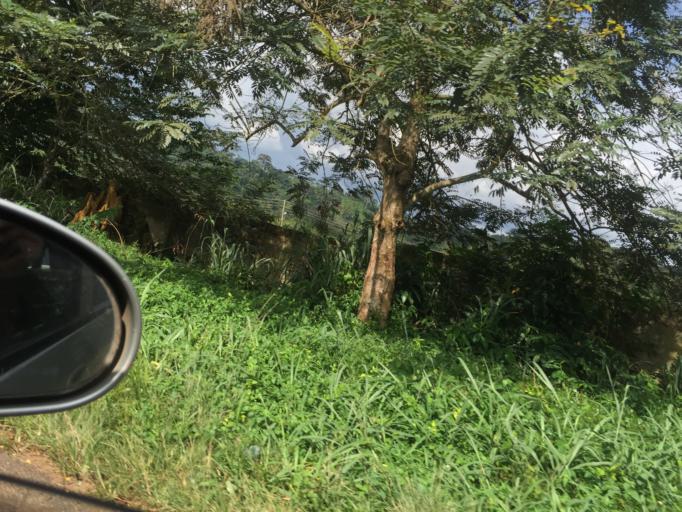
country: GH
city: Mpraeso
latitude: 6.6031
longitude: -0.7396
